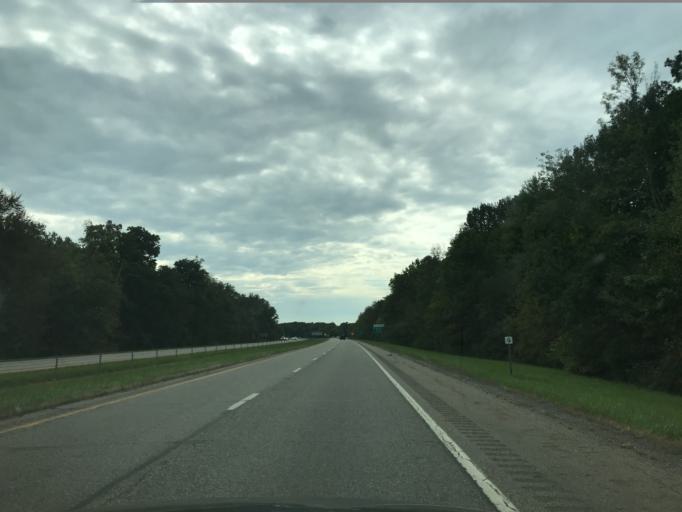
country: US
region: Ohio
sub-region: Trumbull County
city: Howland Center
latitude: 41.2486
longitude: -80.7664
